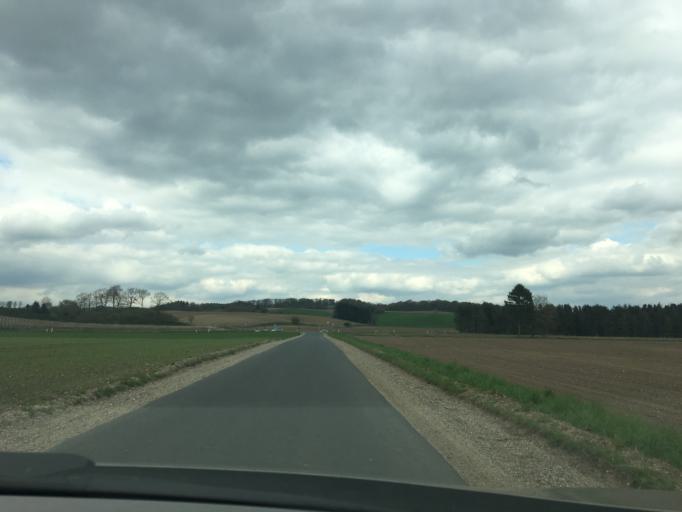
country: DK
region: Central Jutland
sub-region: Horsens Kommune
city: Braedstrup
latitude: 55.9548
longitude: 9.6684
